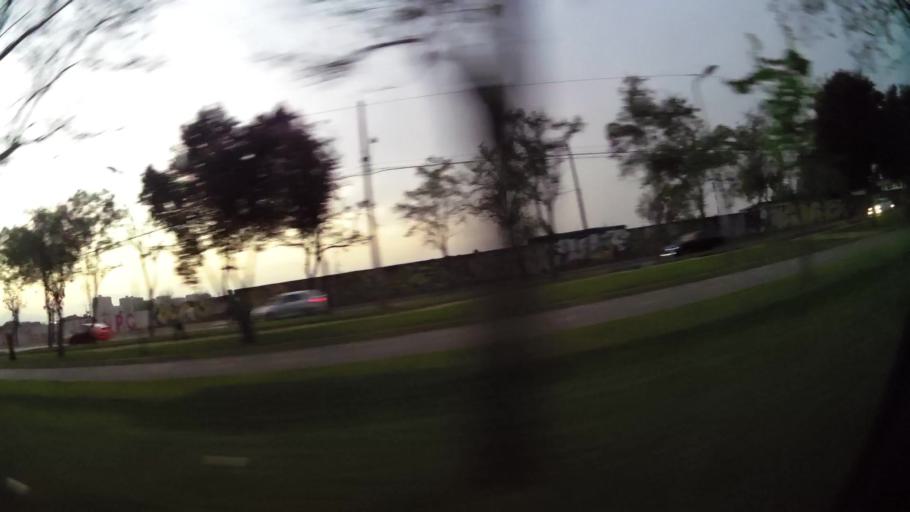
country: CL
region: Santiago Metropolitan
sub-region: Provincia de Santiago
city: Lo Prado
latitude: -33.4690
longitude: -70.7144
